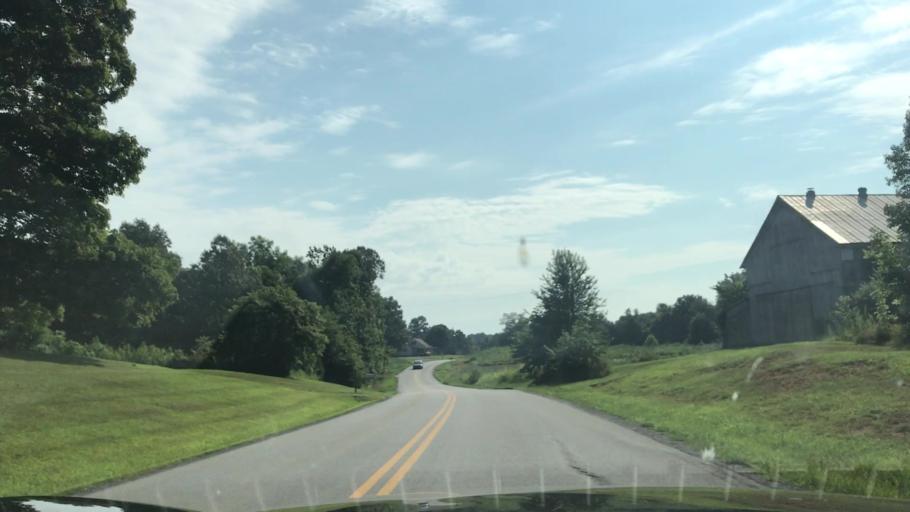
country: US
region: Kentucky
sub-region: Green County
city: Greensburg
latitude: 37.2263
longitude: -85.6552
